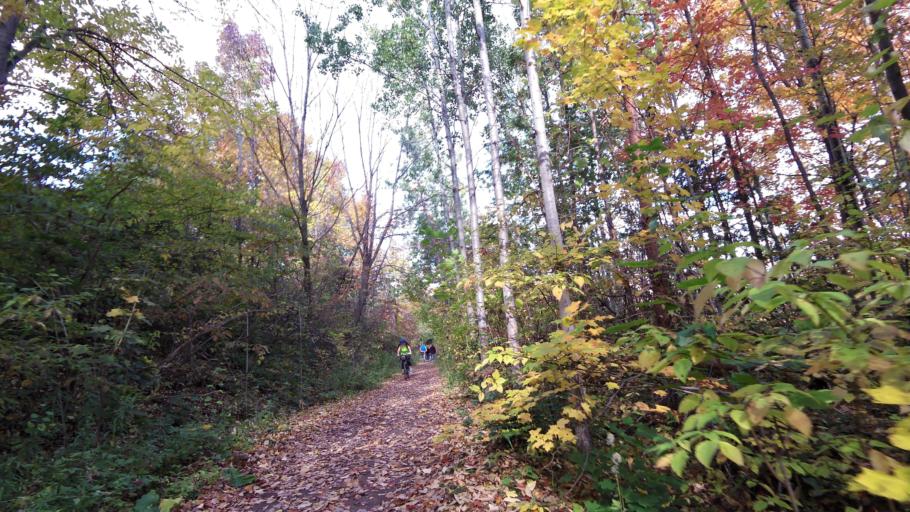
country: CA
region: Ontario
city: Orangeville
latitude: 43.8212
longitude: -80.0235
